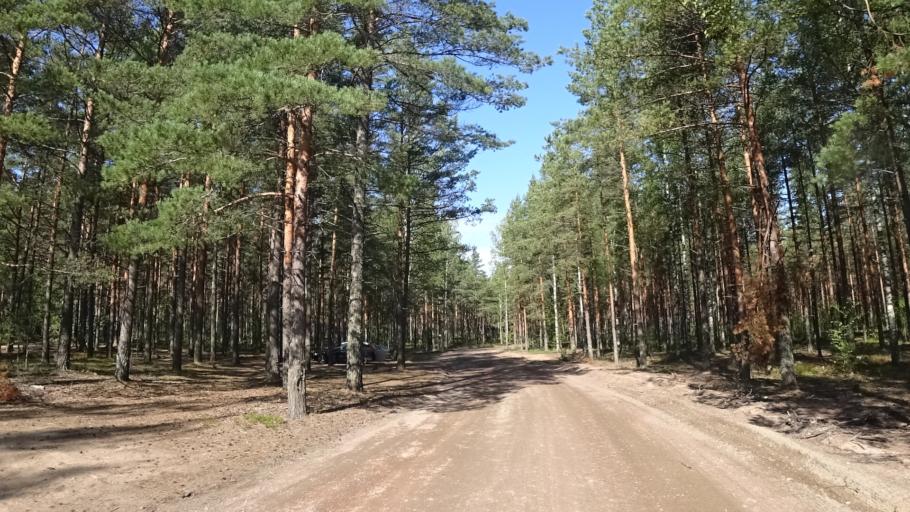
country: FI
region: Kymenlaakso
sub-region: Kotka-Hamina
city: Hamina
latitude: 60.5494
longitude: 27.2039
